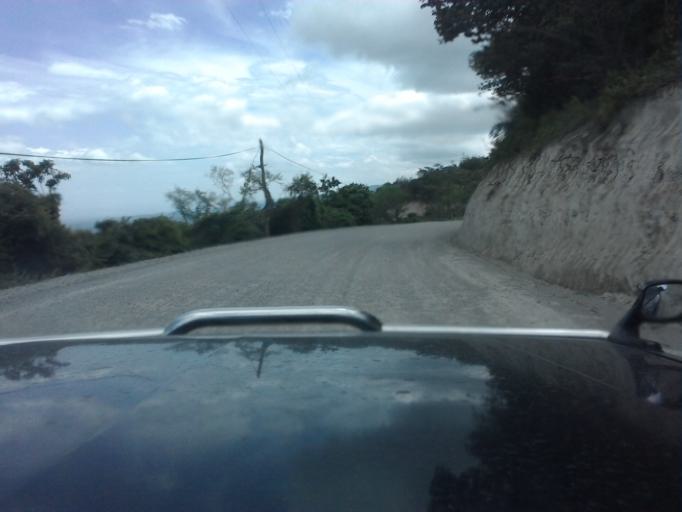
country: CR
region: Guanacaste
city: Juntas
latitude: 10.2729
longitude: -84.8394
